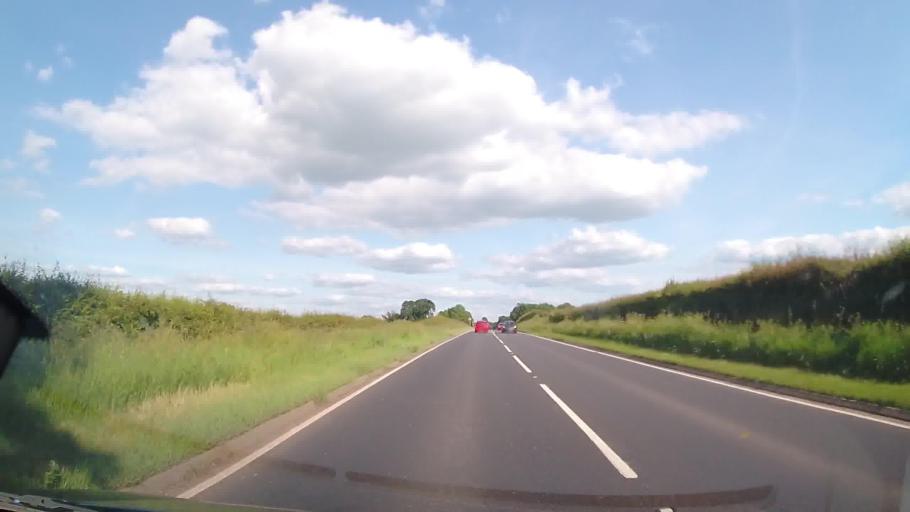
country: GB
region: England
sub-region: Shropshire
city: Westbury
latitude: 52.7022
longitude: -2.9969
